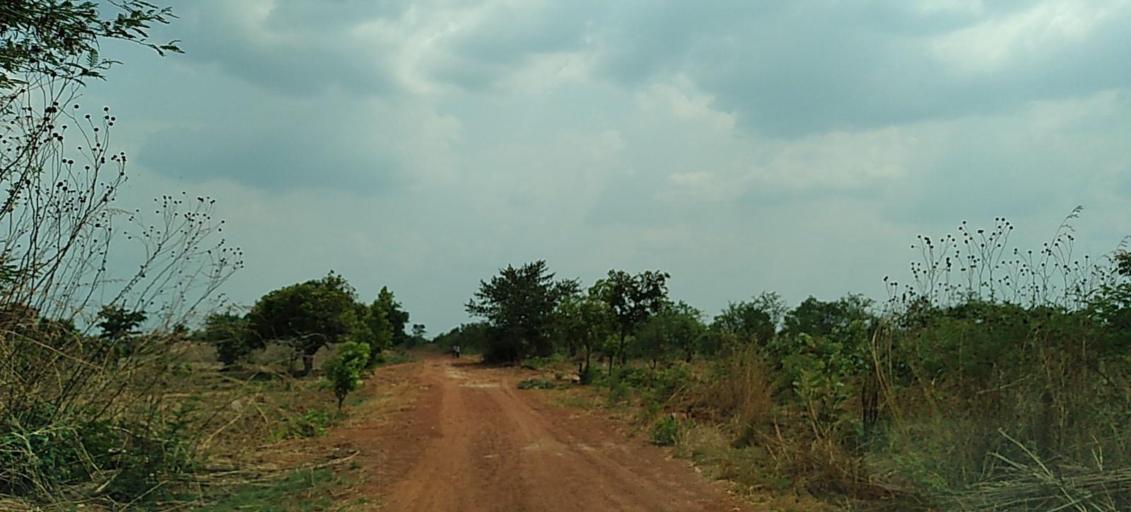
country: ZM
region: Copperbelt
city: Kalulushi
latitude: -12.8768
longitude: 28.0748
